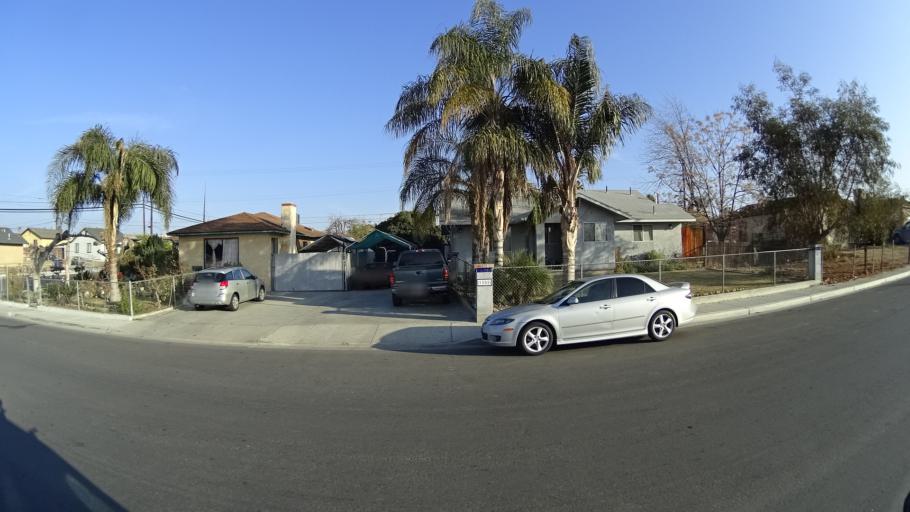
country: US
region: California
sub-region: Kern County
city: Bakersfield
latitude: 35.3821
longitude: -118.9772
